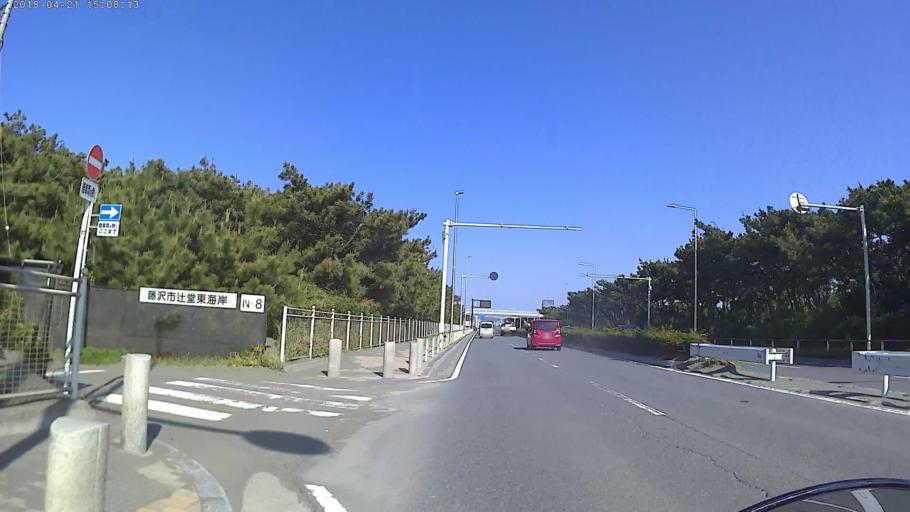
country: JP
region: Kanagawa
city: Fujisawa
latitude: 35.3187
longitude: 139.4561
